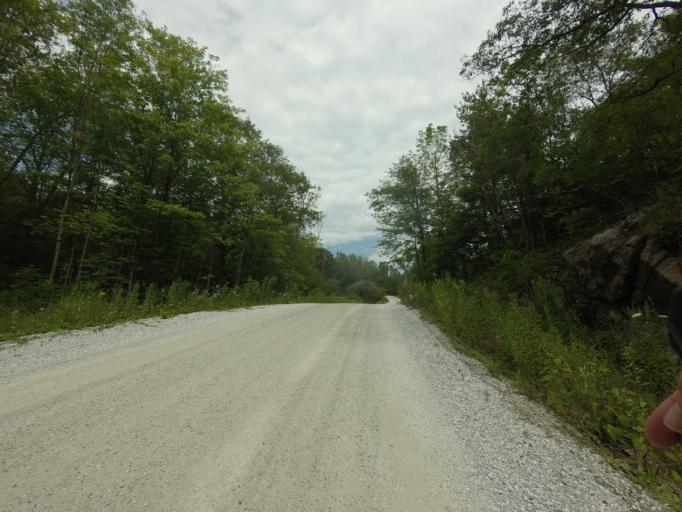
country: CA
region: Ontario
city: Perth
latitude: 44.7360
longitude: -76.6086
